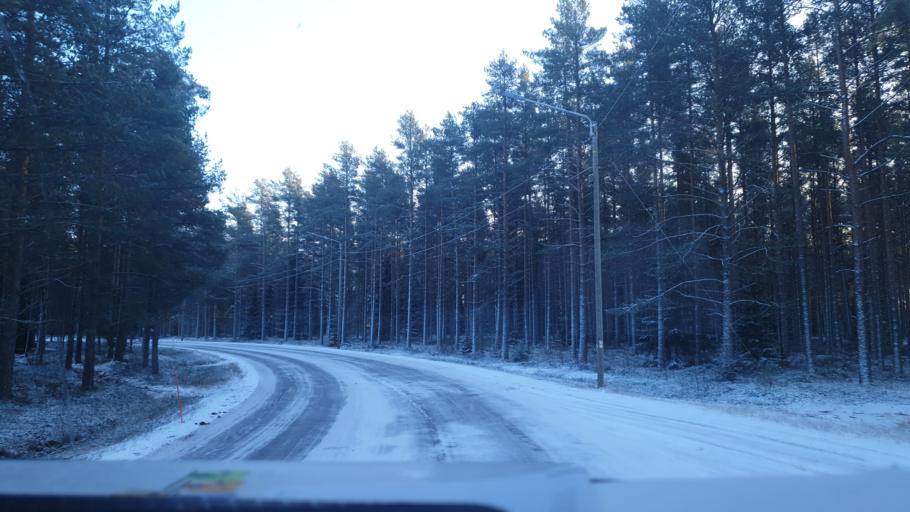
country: FI
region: Central Ostrobothnia
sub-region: Kokkola
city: Kokkola
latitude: 63.8197
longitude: 23.0710
